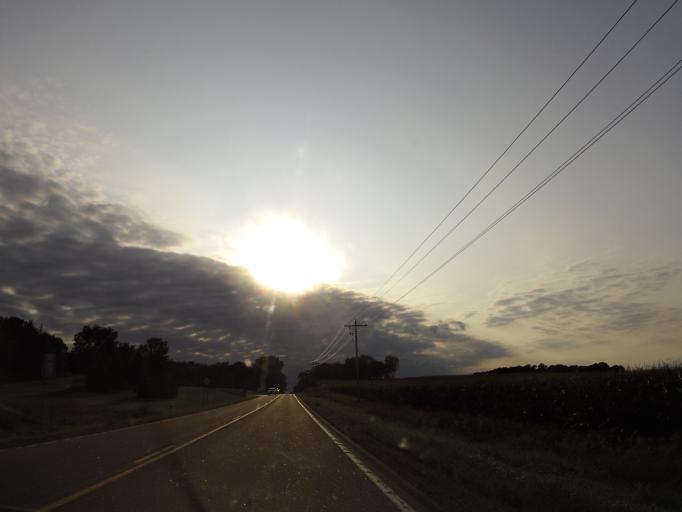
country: US
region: Minnesota
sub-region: Dakota County
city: Farmington
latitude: 44.6304
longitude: -93.0269
